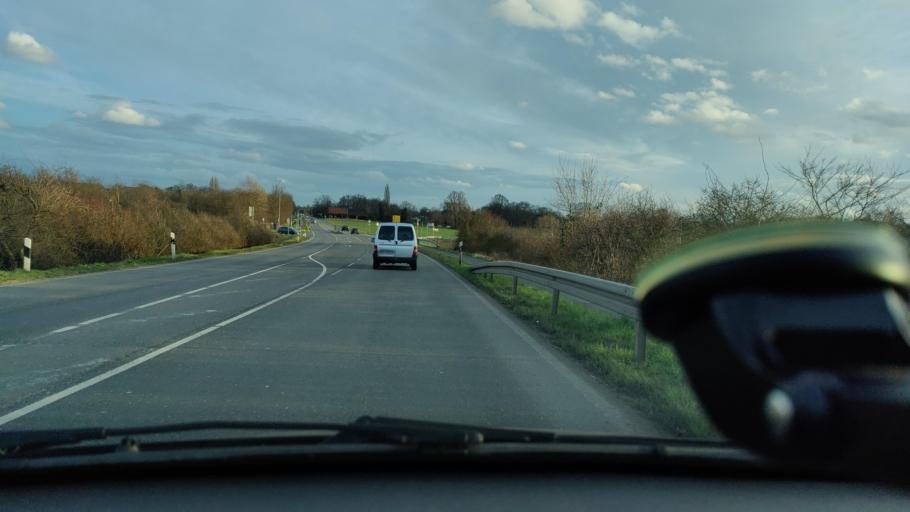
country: DE
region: North Rhine-Westphalia
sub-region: Regierungsbezirk Dusseldorf
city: Kamp-Lintfort
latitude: 51.4895
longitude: 6.5839
